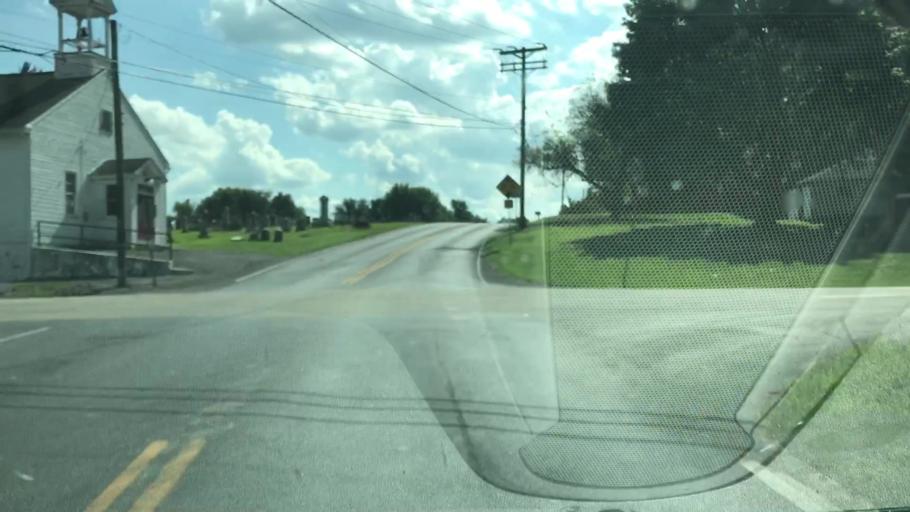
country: US
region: Pennsylvania
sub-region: Dauphin County
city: Middletown
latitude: 40.1726
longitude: -76.7042
